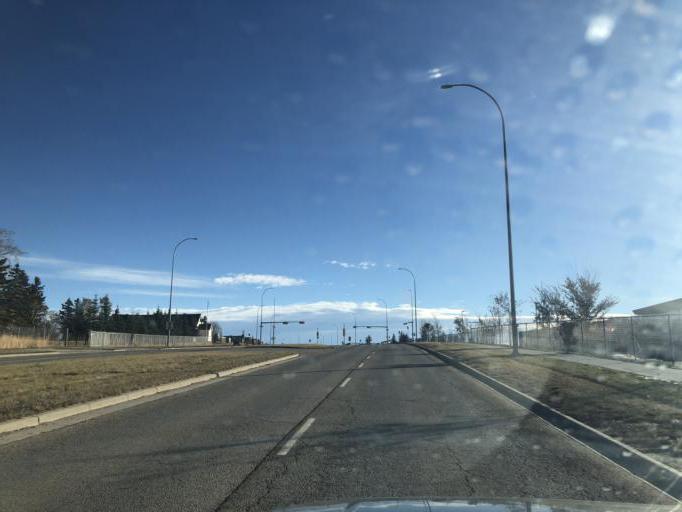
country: CA
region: Alberta
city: Calgary
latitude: 51.0378
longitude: -114.1962
